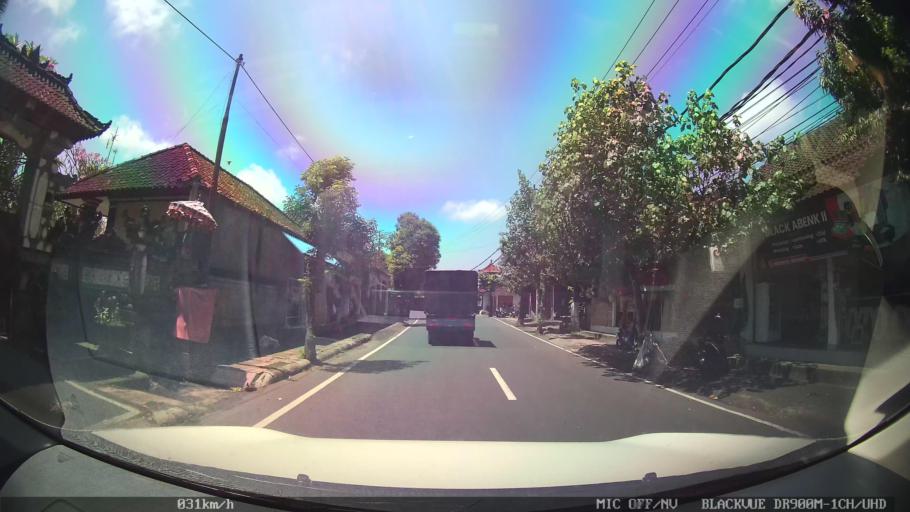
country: ID
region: Bali
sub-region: Kabupaten Gianyar
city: Ubud
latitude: -8.5583
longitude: 115.3139
